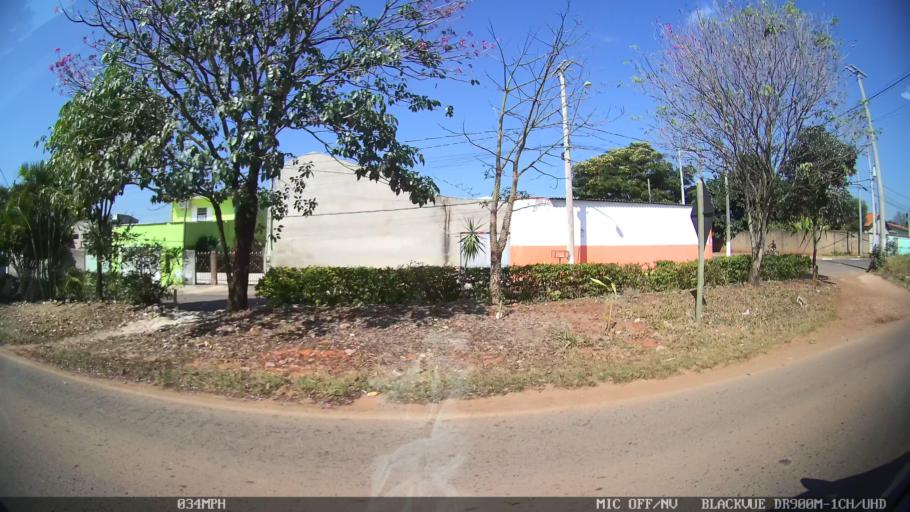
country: BR
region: Sao Paulo
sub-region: Indaiatuba
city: Indaiatuba
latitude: -23.0329
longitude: -47.1036
